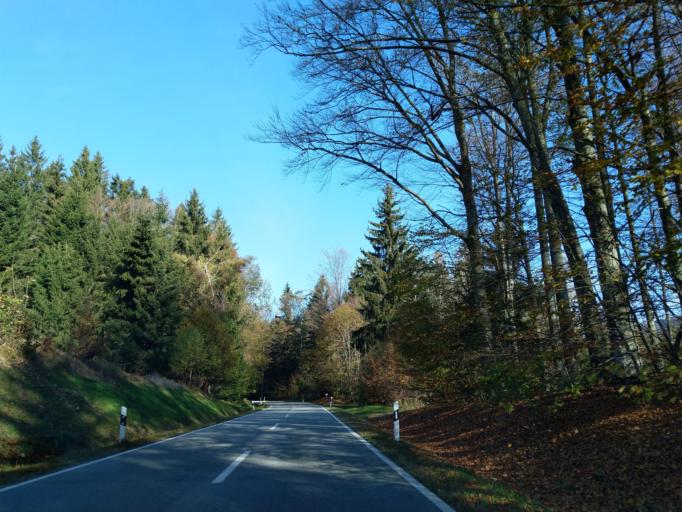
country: DE
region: Bavaria
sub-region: Lower Bavaria
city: Grattersdorf
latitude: 48.8093
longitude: 13.1880
